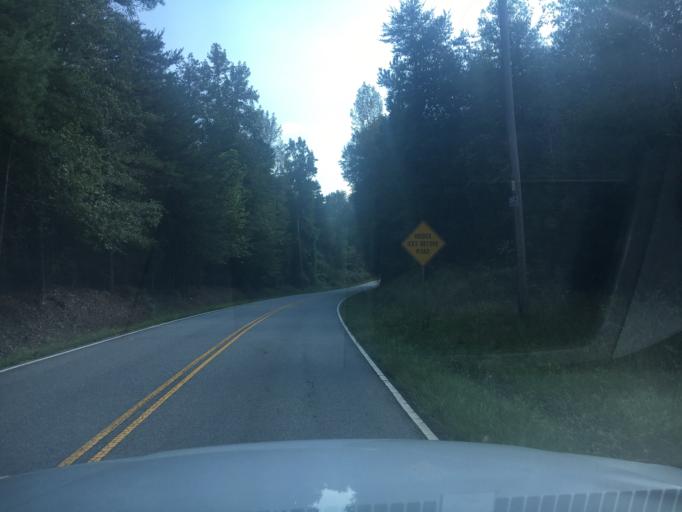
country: US
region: South Carolina
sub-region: Pickens County
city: Liberty
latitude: 34.7087
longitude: -82.6382
